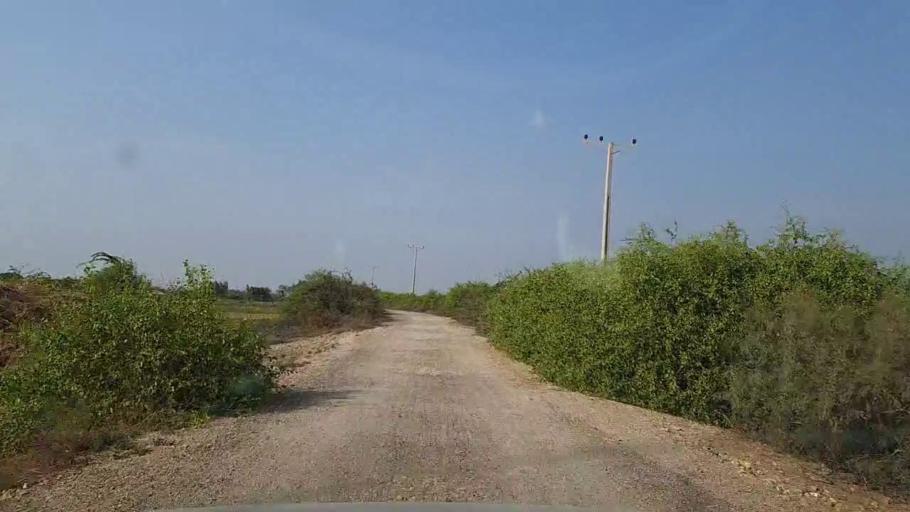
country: PK
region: Sindh
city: Mirpur Sakro
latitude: 24.5773
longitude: 67.5692
